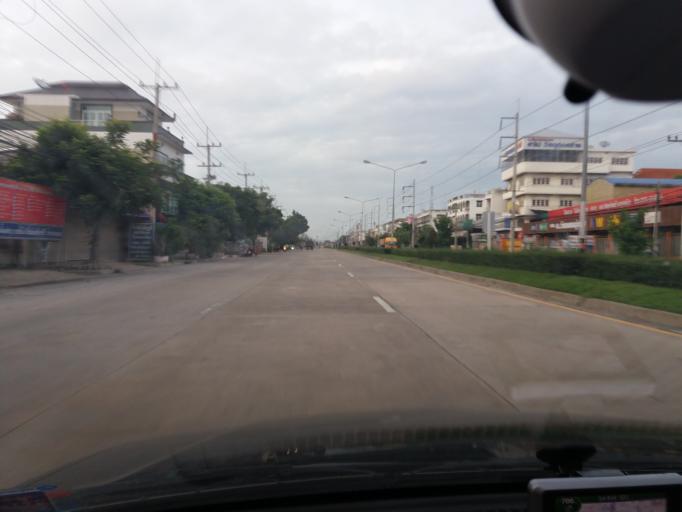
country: TH
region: Suphan Buri
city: U Thong
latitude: 14.3839
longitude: 99.8947
